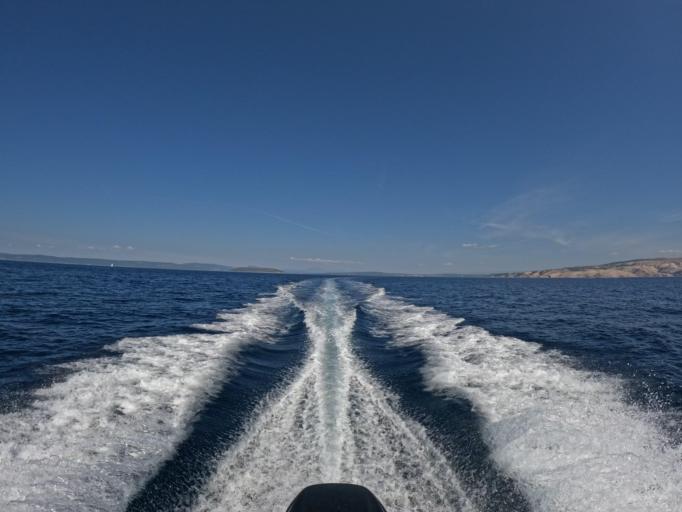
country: HR
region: Primorsko-Goranska
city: Punat
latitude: 44.9069
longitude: 14.6307
